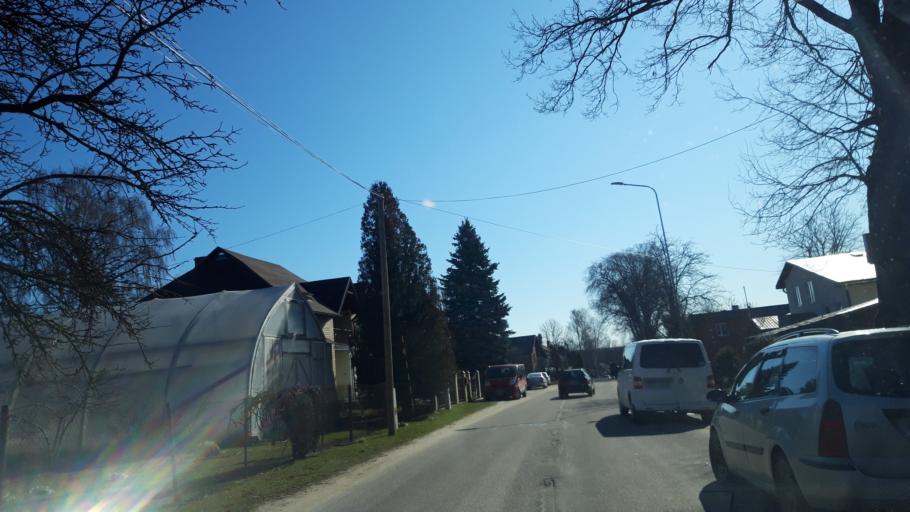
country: LV
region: Valmieras Rajons
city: Valmiera
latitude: 57.5473
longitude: 25.4528
